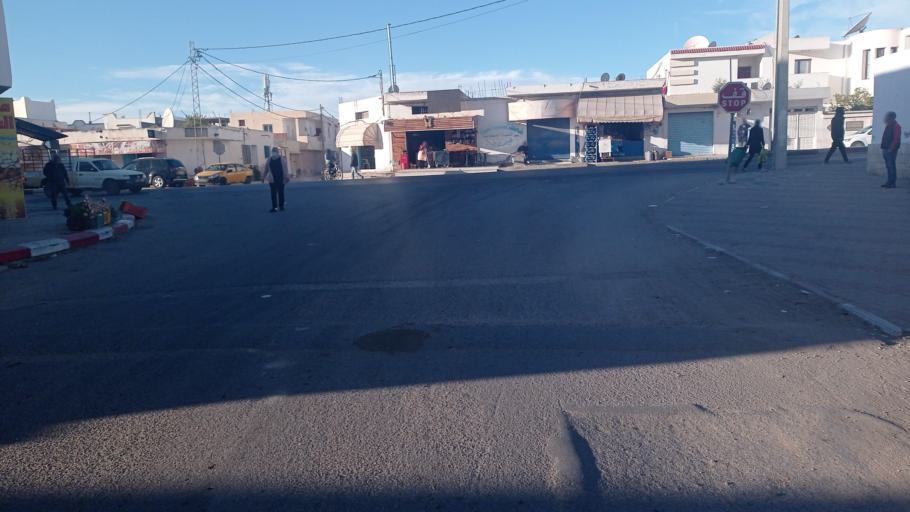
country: TN
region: Qabis
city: Gabes
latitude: 33.8399
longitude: 10.1156
